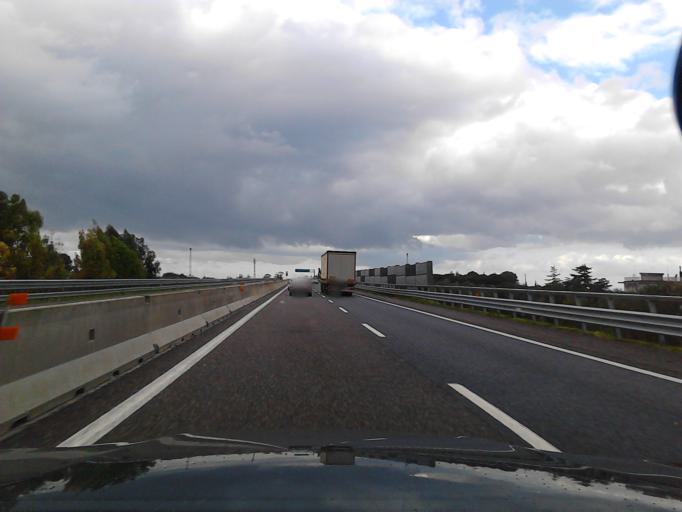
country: IT
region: Apulia
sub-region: Provincia di Bari
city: Molfetta
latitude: 41.1743
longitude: 16.5825
